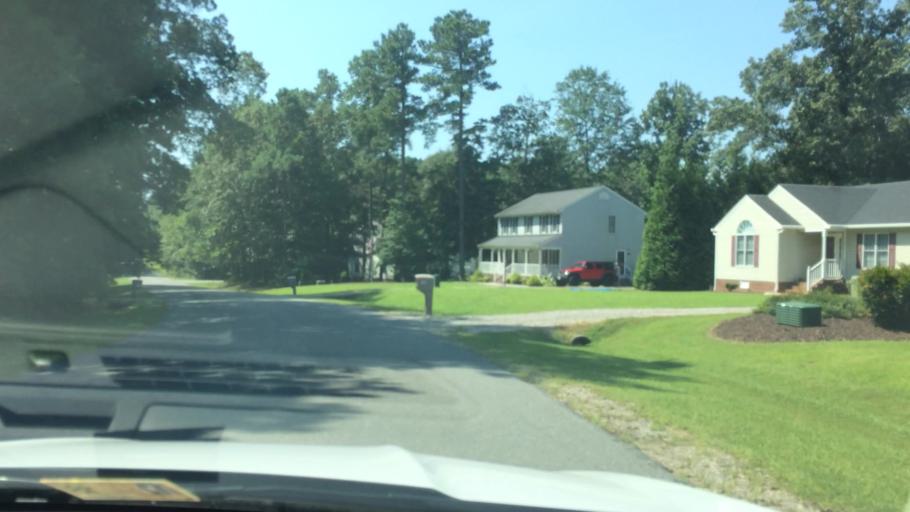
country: US
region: Virginia
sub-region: Henrico County
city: Sandston
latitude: 37.5095
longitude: -77.1612
